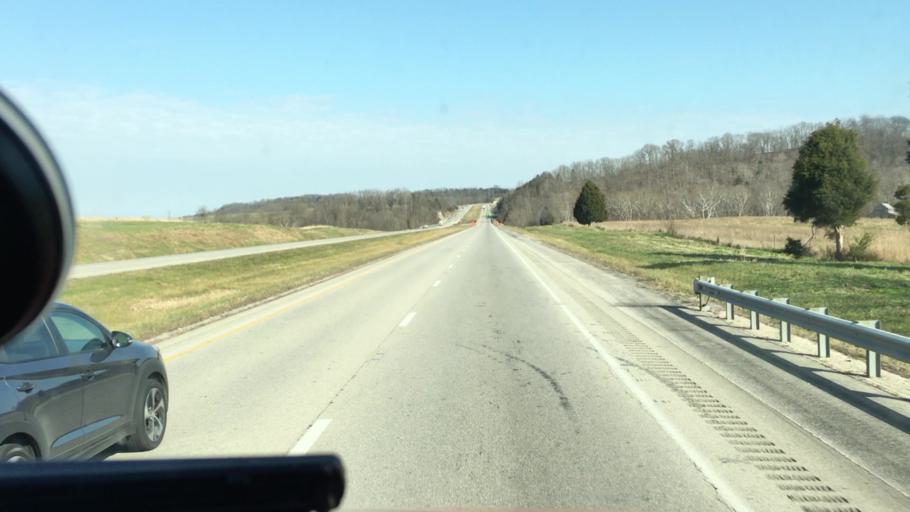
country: US
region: Kentucky
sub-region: Bath County
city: Owingsville
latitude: 38.1141
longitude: -83.8037
